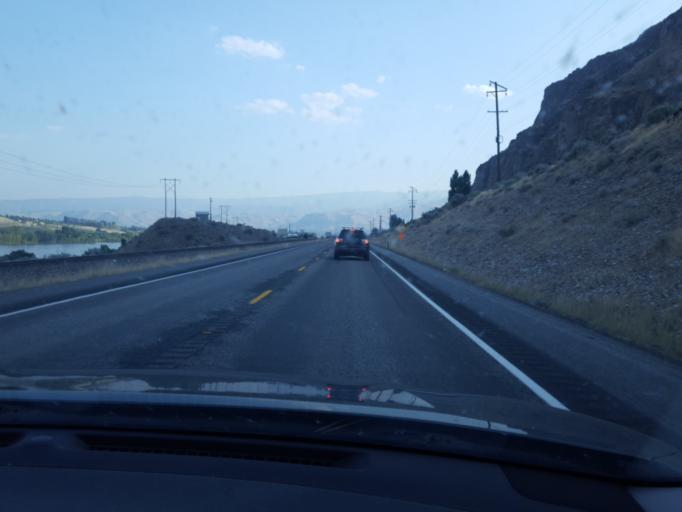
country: US
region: Washington
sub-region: Chelan County
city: Sunnyslope
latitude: 47.5004
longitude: -120.3116
